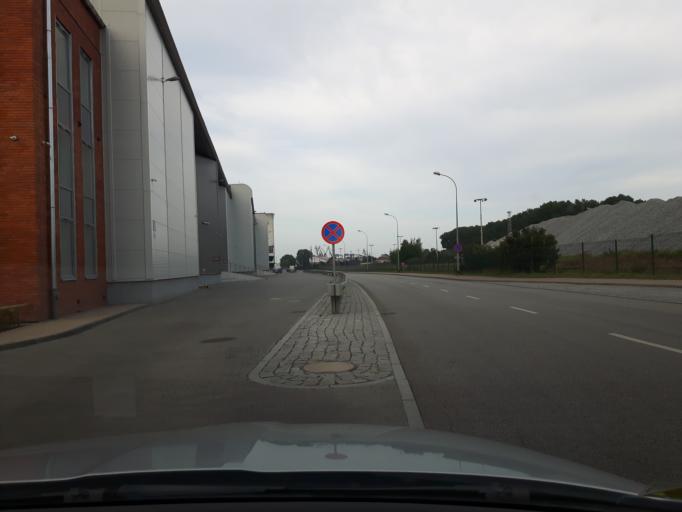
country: PL
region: Pomeranian Voivodeship
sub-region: Gdynia
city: Gdynia
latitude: 54.5271
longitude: 18.5312
